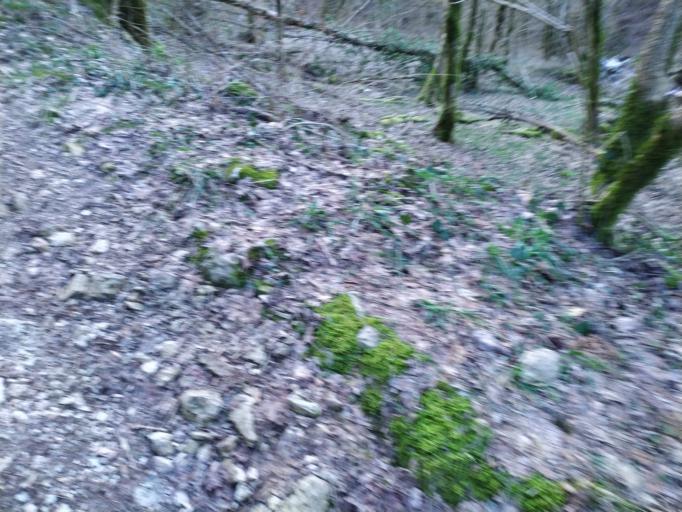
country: IT
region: Veneto
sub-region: Provincia di Vicenza
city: Monte di Malo
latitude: 45.6784
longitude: 11.3493
